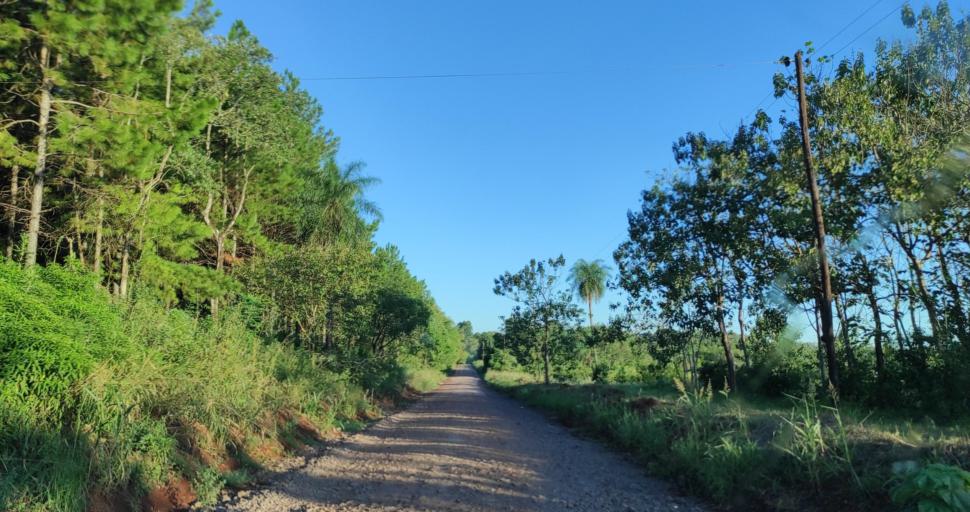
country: AR
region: Misiones
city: Gobernador Roca
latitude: -27.2019
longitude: -55.4594
